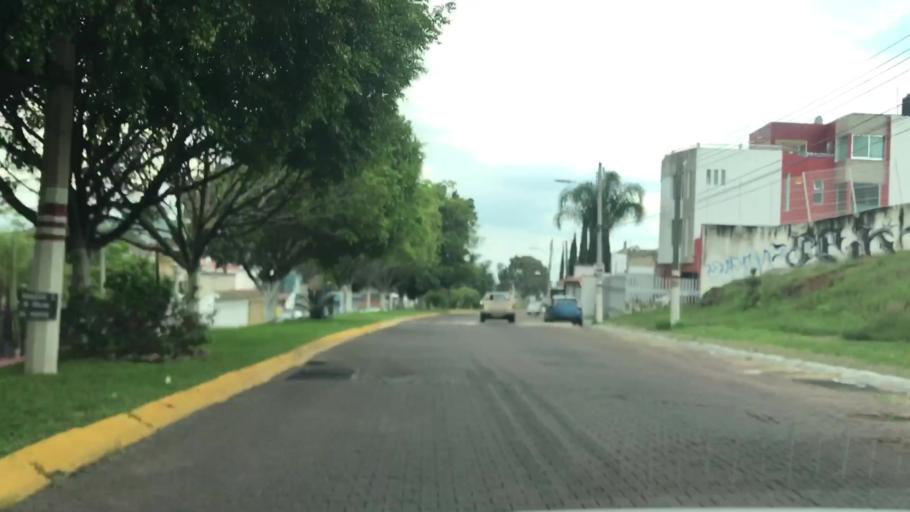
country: MX
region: Jalisco
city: Guadalajara
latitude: 20.6181
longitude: -103.4035
